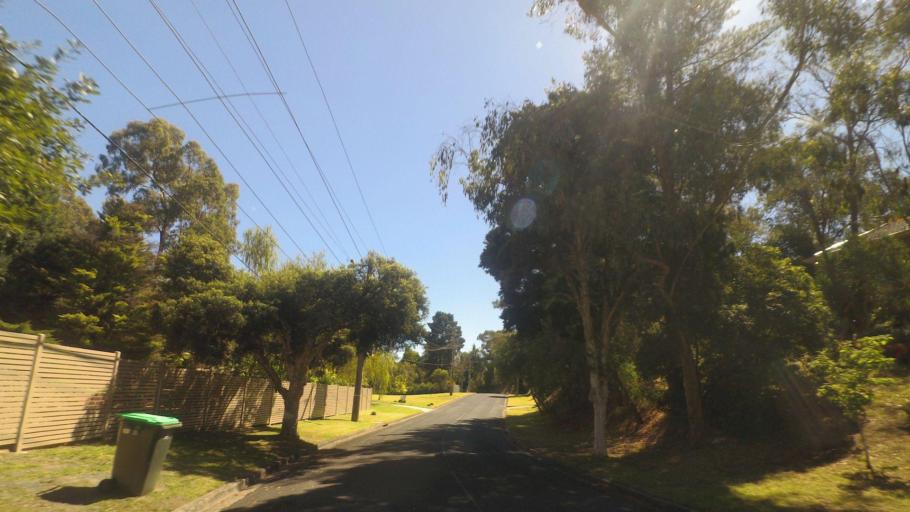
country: AU
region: Victoria
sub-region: Manningham
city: Donvale
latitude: -37.7940
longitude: 145.1943
